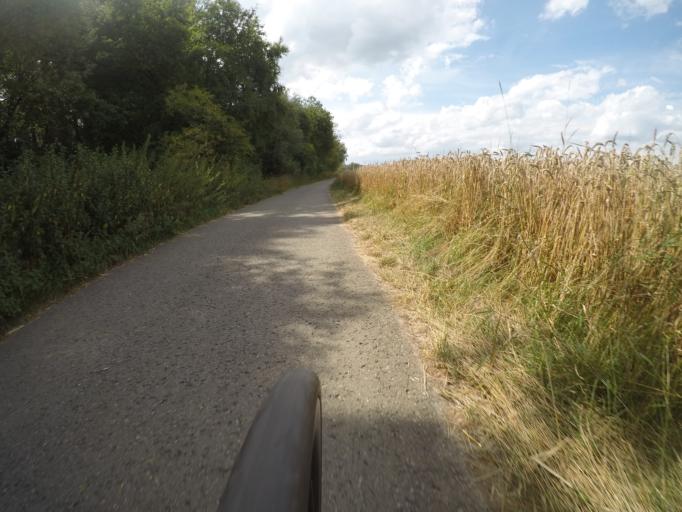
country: DE
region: Baden-Wuerttemberg
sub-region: Regierungsbezirk Stuttgart
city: Weil der Stadt
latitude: 48.7624
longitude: 8.8652
